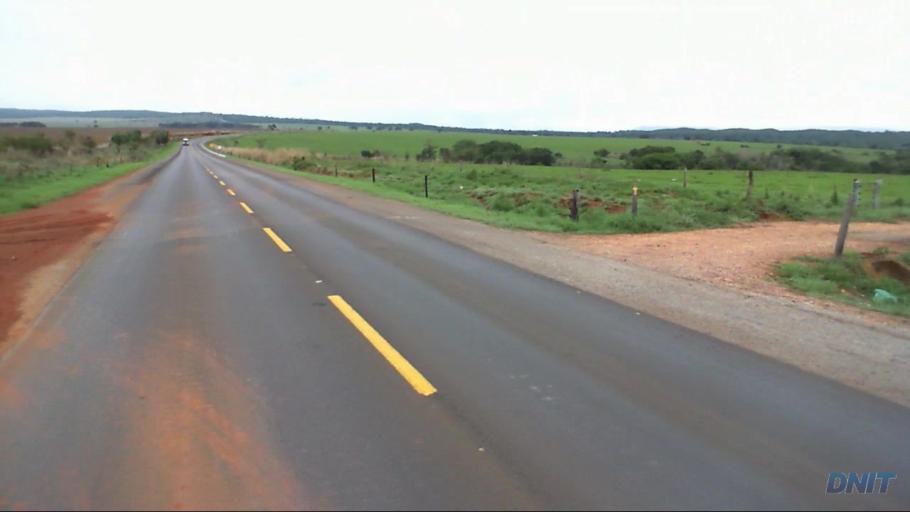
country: BR
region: Goias
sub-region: Padre Bernardo
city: Padre Bernardo
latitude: -15.1744
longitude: -48.3750
